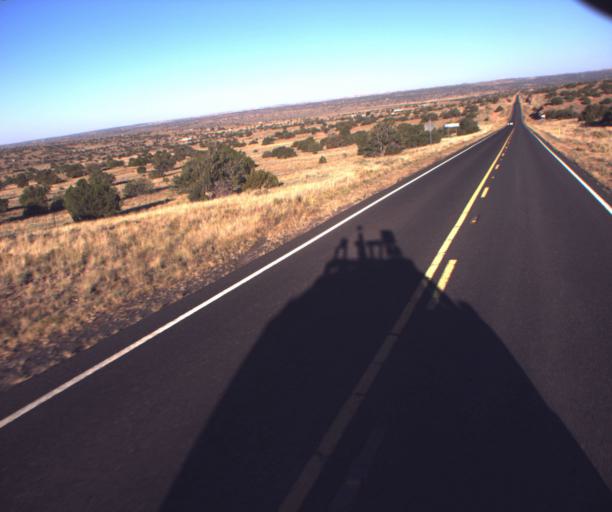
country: US
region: Arizona
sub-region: Apache County
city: Houck
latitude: 35.3645
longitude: -109.4711
